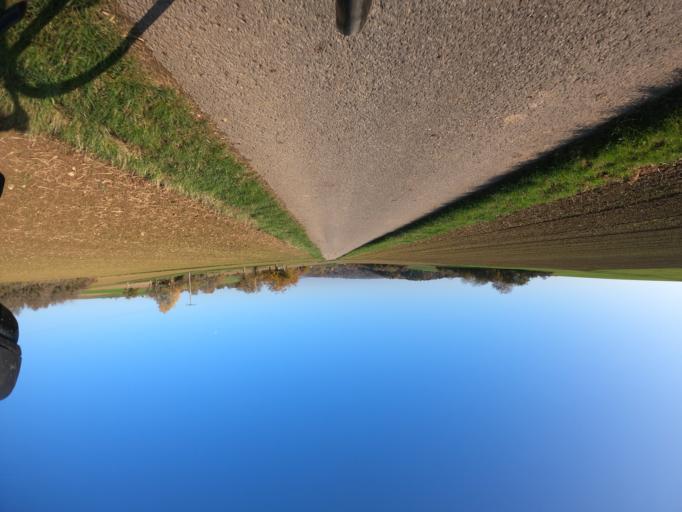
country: DE
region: Baden-Wuerttemberg
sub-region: Regierungsbezirk Stuttgart
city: Weil der Stadt
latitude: 48.7412
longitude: 8.8962
